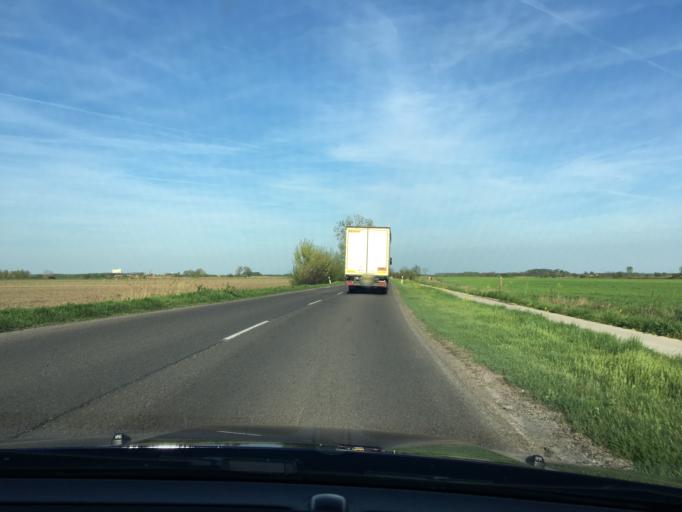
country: HU
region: Bekes
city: Korosladany
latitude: 47.0000
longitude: 21.1057
